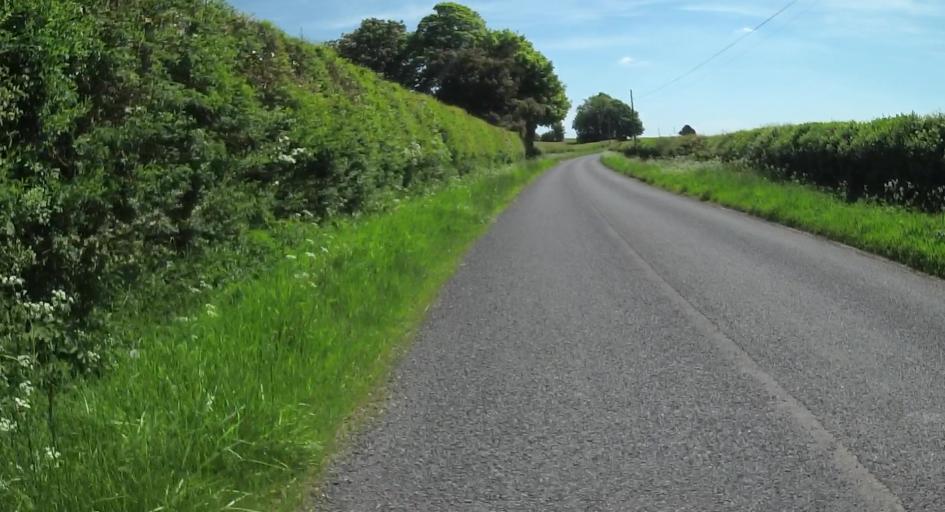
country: GB
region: England
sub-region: Hampshire
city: Four Marks
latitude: 51.1625
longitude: -1.1354
